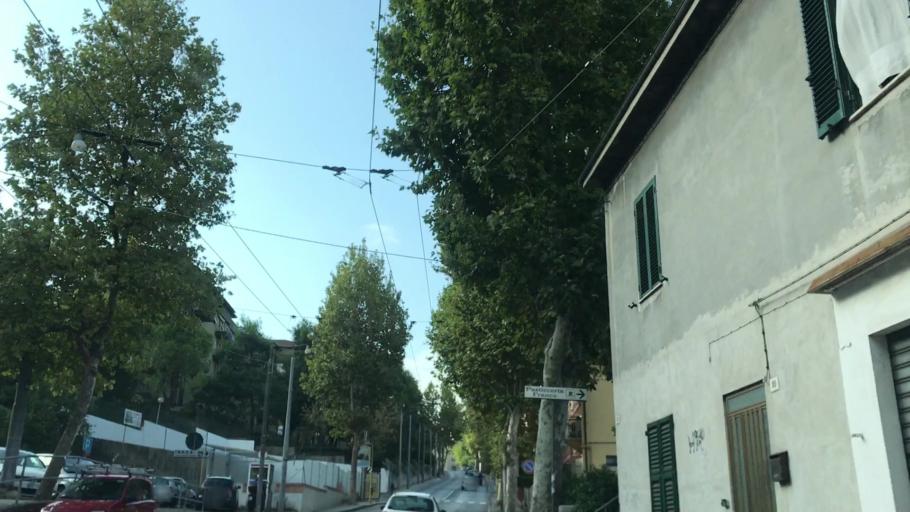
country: IT
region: The Marches
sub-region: Provincia di Ancona
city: Le Grazie di Ancona
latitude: 43.5965
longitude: 13.5174
